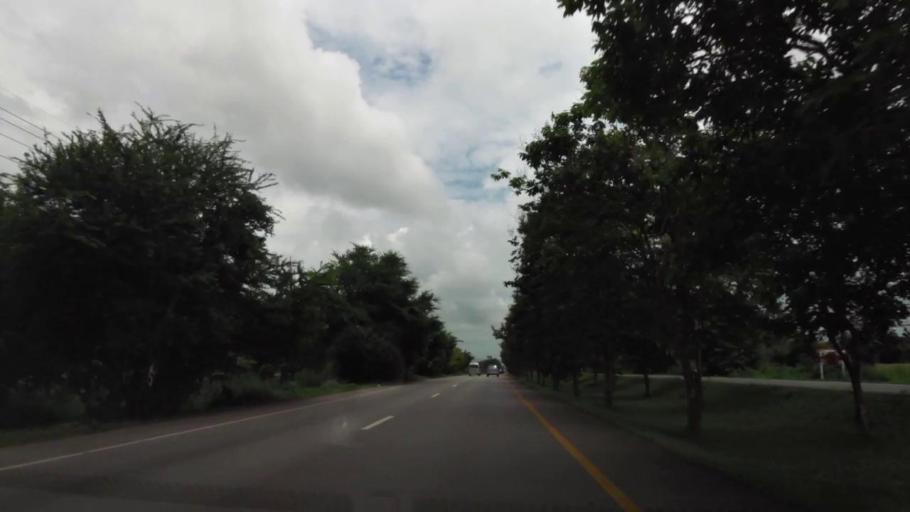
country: TH
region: Chanthaburi
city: Na Yai Am
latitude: 12.7490
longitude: 101.8750
